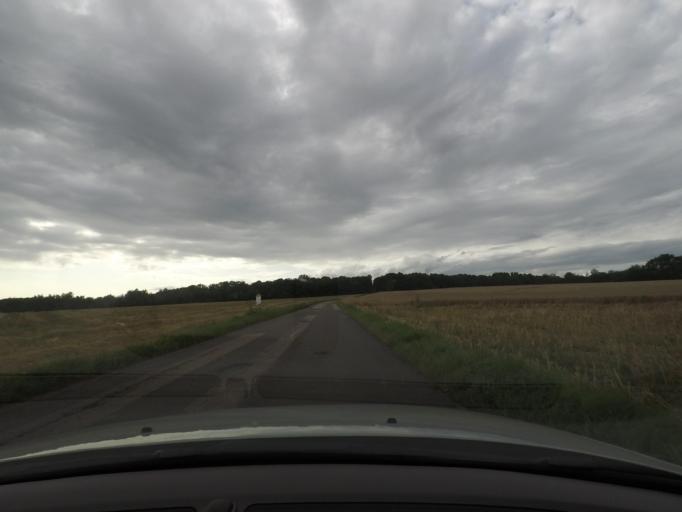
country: FR
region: Haute-Normandie
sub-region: Departement de l'Eure
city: Le Manoir
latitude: 49.3299
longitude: 1.2102
